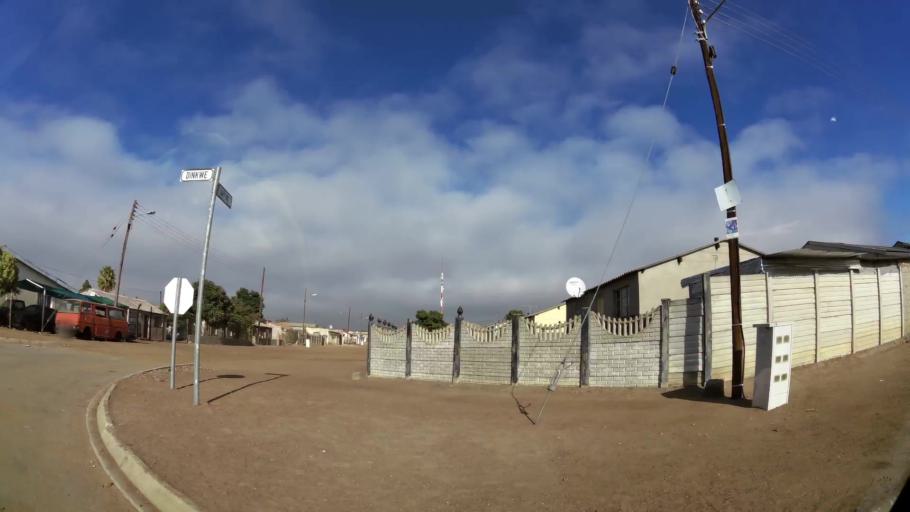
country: ZA
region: Limpopo
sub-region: Capricorn District Municipality
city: Polokwane
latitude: -23.8446
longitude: 29.3922
